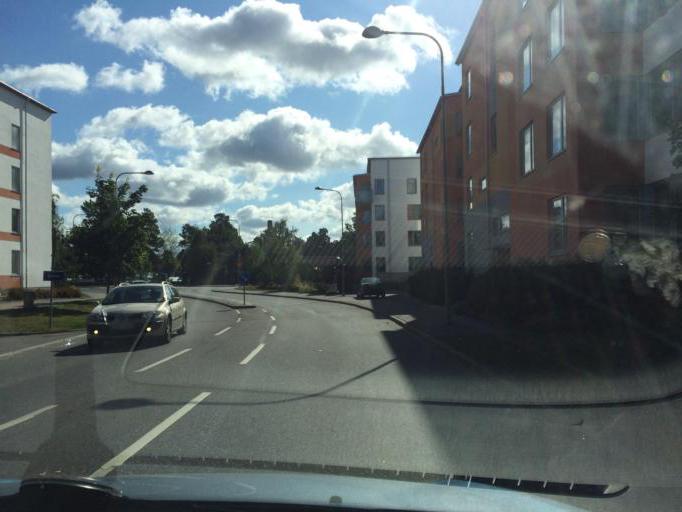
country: SE
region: Stockholm
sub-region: Nacka Kommun
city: Nacka
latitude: 59.2809
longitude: 18.1254
